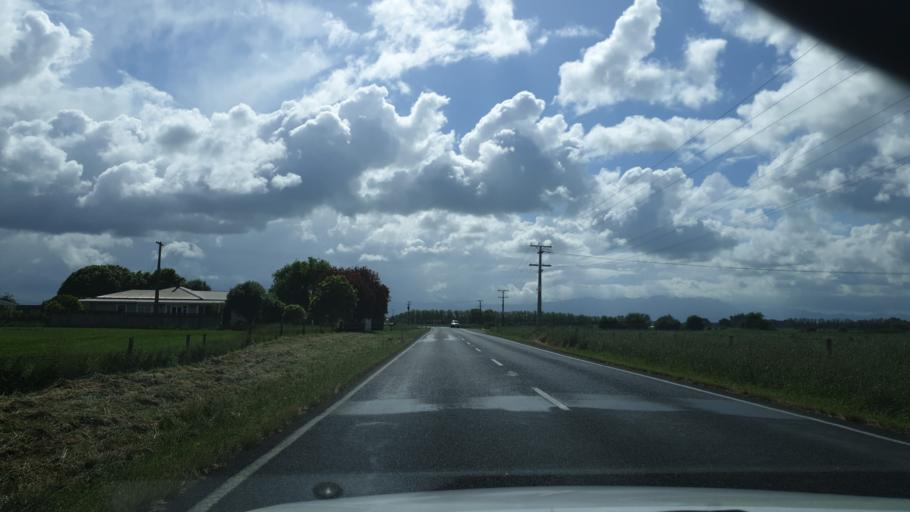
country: NZ
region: Waikato
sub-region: Hauraki District
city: Paeroa
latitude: -37.5131
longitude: 175.5129
